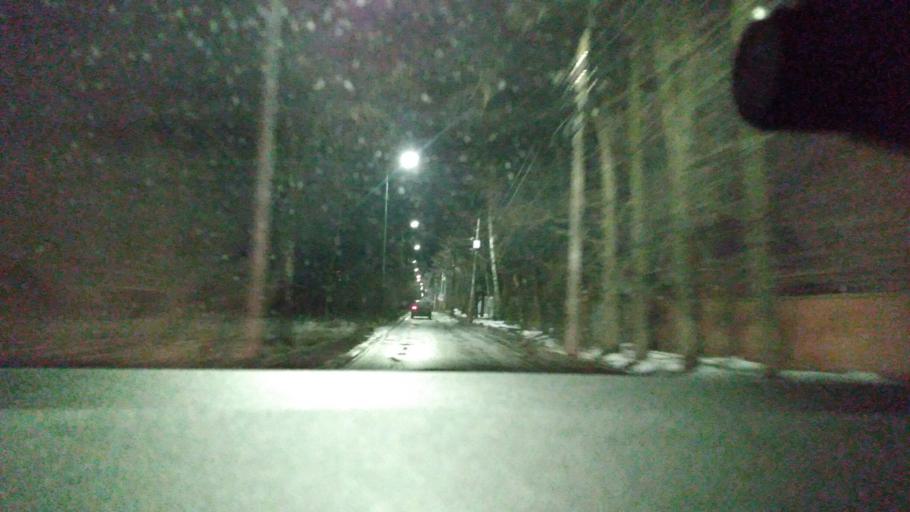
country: RU
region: Moskovskaya
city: Saltykovka
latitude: 55.7571
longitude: 37.9384
